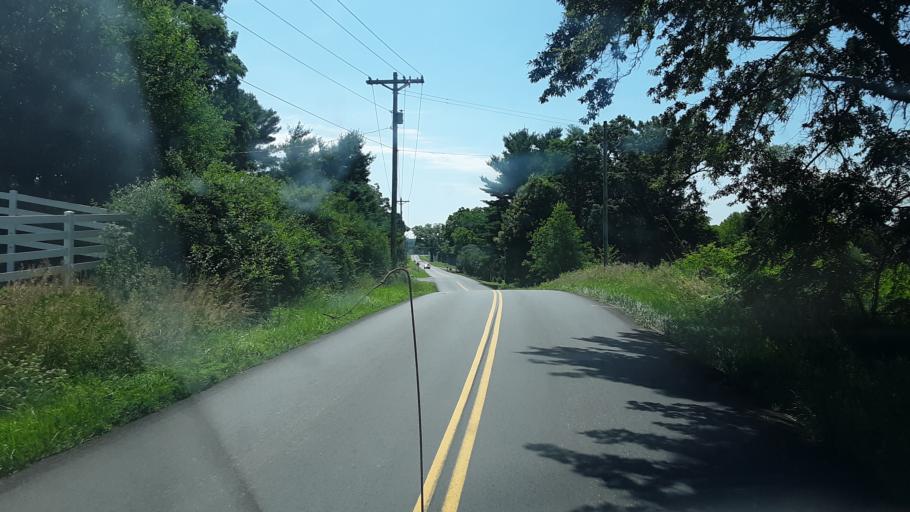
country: US
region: Ohio
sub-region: Wayne County
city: Shreve
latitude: 40.7361
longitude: -82.0637
